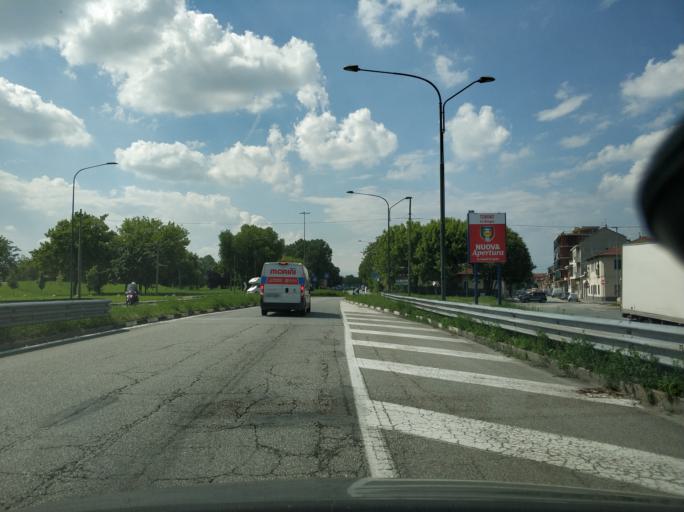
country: IT
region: Piedmont
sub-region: Provincia di Torino
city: San Mauro Torinese
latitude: 45.0961
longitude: 7.7273
